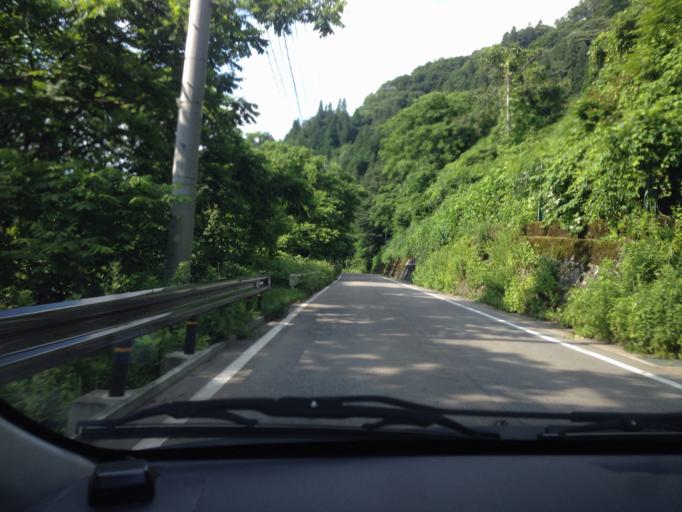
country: JP
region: Fukushima
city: Kitakata
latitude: 37.4467
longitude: 139.5256
